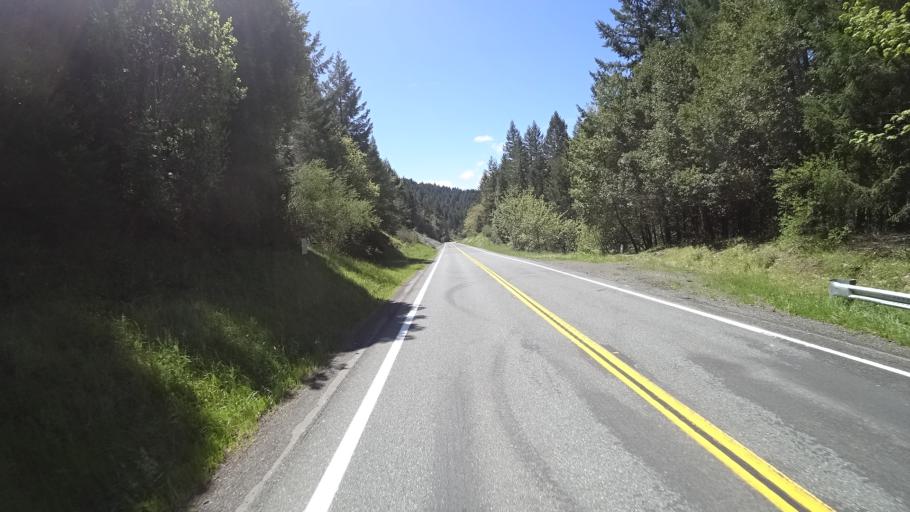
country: US
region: California
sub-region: Humboldt County
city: Willow Creek
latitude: 40.9189
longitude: -123.7952
